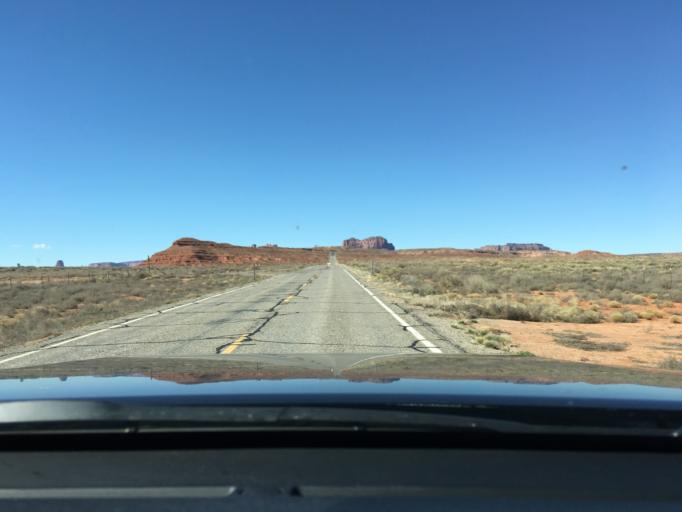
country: US
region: Arizona
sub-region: Navajo County
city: Kayenta
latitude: 37.0892
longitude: -110.0093
